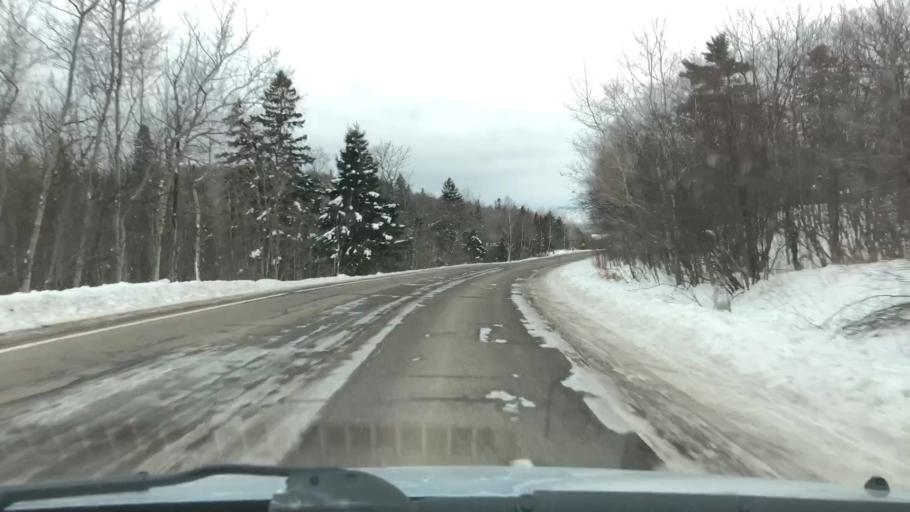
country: US
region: Minnesota
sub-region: Saint Louis County
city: Proctor
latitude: 46.7105
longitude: -92.2636
